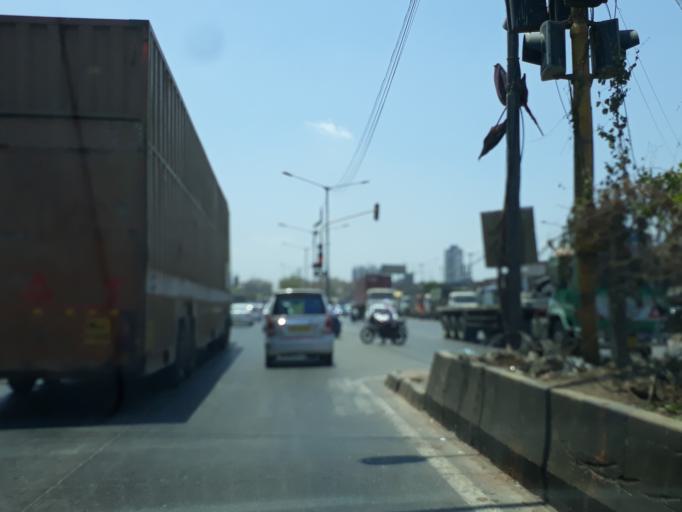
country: IN
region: Maharashtra
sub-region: Mumbai Suburban
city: Mumbai
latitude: 19.0576
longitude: 72.9268
